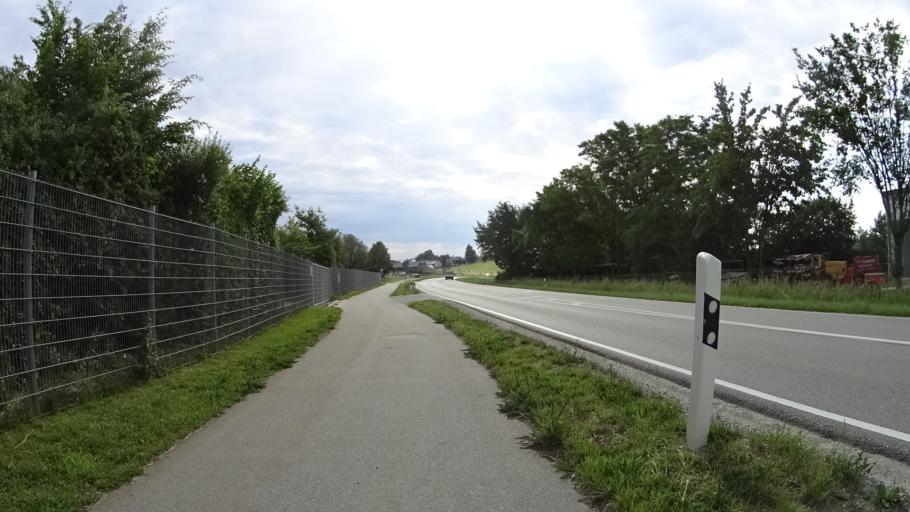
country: DE
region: Bavaria
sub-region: Lower Bavaria
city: Bogen
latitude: 48.8976
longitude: 12.7191
